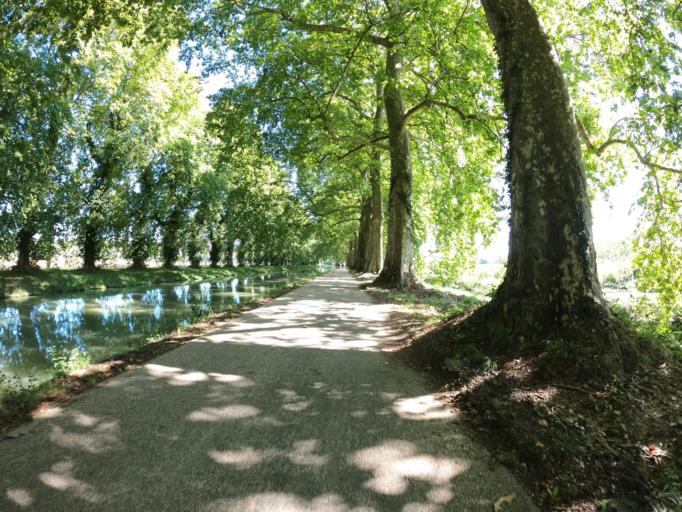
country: FR
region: Midi-Pyrenees
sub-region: Departement du Tarn-et-Garonne
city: Auvillar
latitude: 44.0911
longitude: 0.9593
